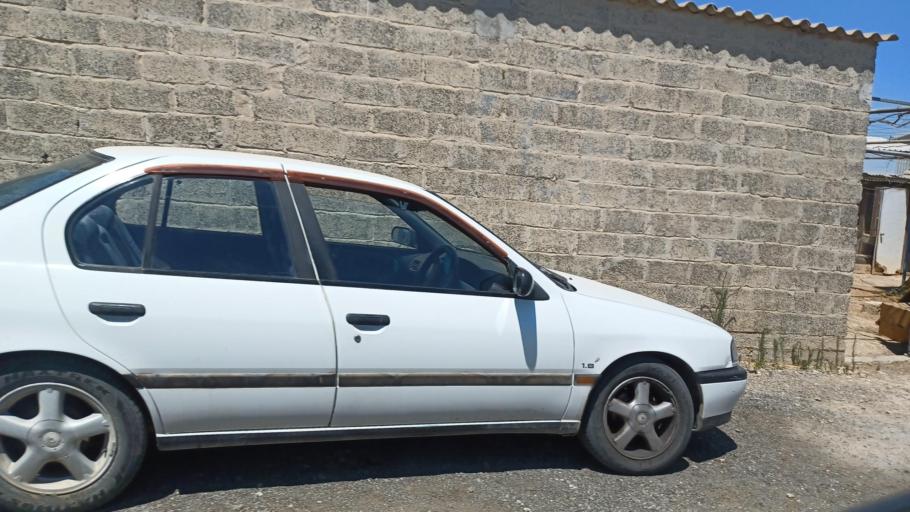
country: CY
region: Ammochostos
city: Acheritou
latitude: 35.0758
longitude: 33.8856
